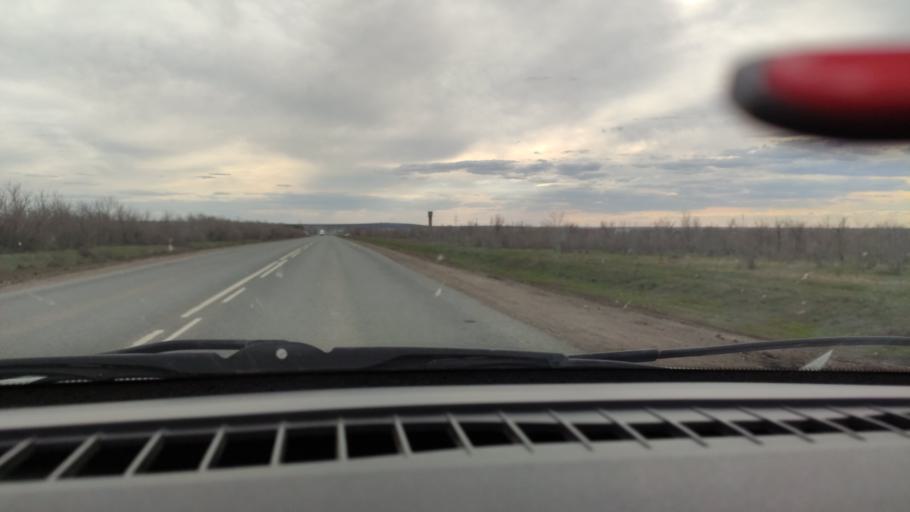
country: RU
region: Bashkortostan
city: Mayachnyy
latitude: 52.3408
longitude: 55.5316
